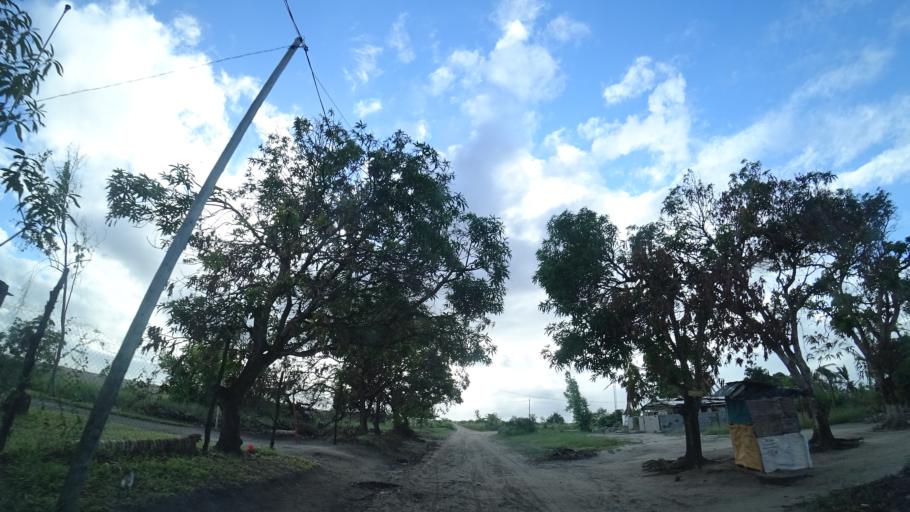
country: MZ
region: Sofala
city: Beira
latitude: -19.7138
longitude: 35.0114
